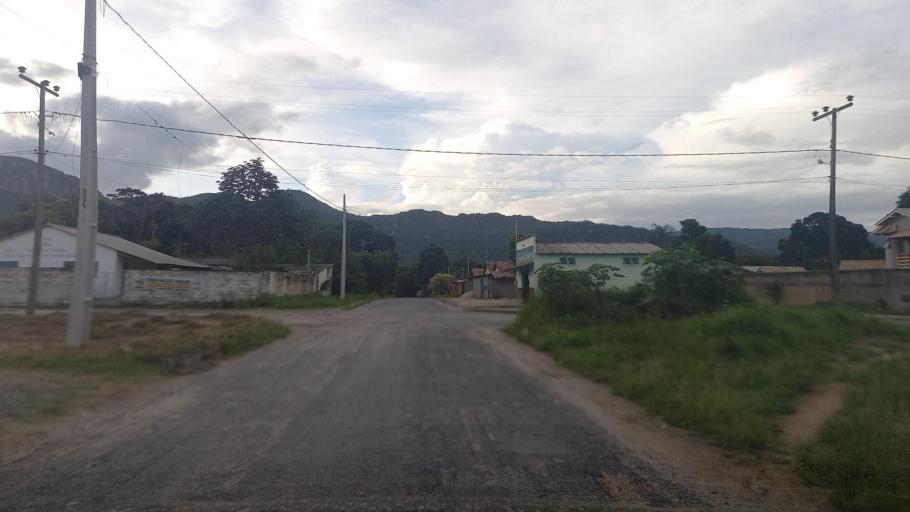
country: BR
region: Goias
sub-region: Cavalcante
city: Cavalcante
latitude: -13.7901
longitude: -47.4590
